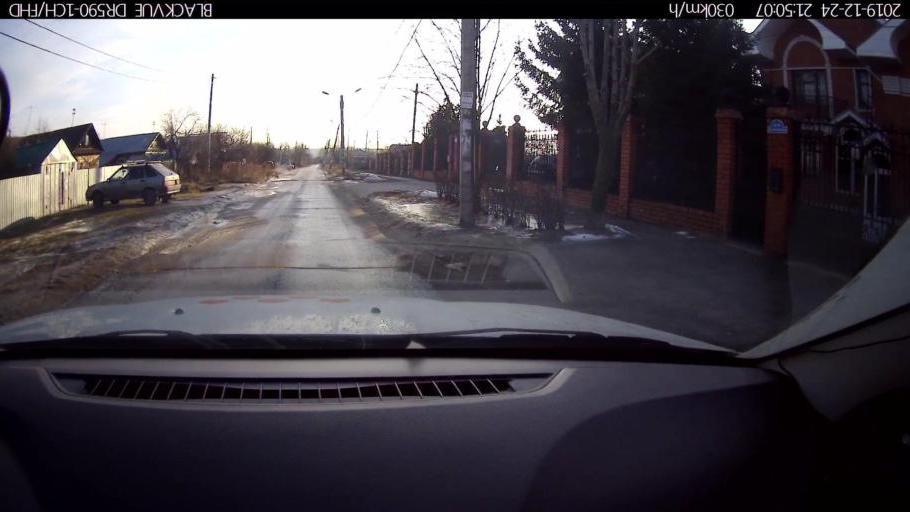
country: RU
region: Nizjnij Novgorod
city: Burevestnik
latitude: 56.2226
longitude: 43.8443
